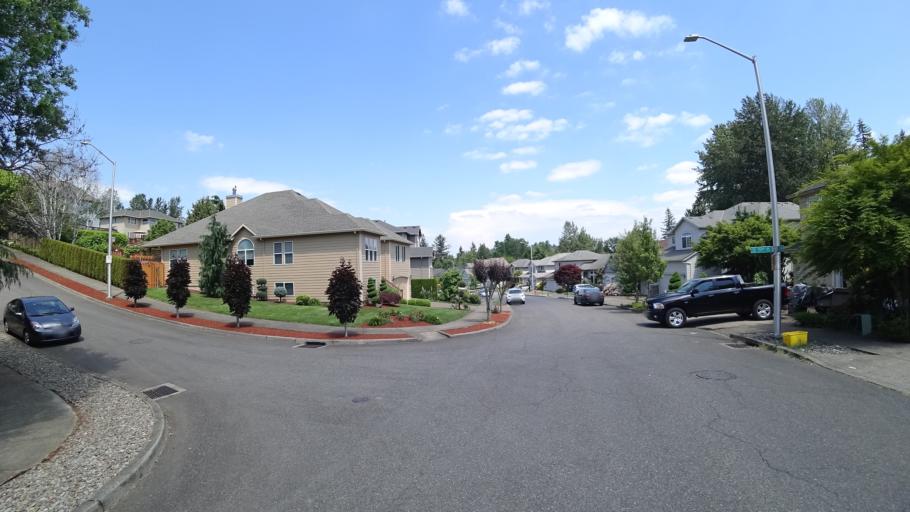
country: US
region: Oregon
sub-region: Clackamas County
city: Happy Valley
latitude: 45.4689
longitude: -122.4983
